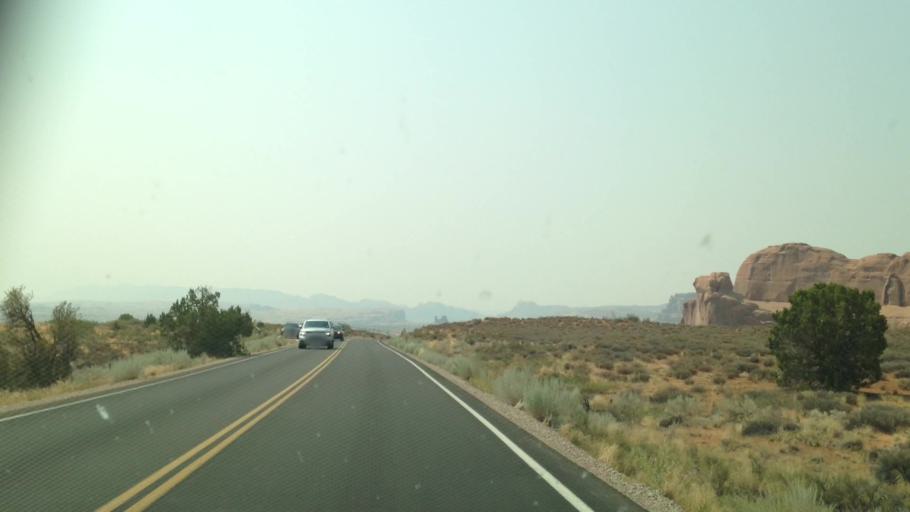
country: US
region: Utah
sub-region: Grand County
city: Moab
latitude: 38.6667
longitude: -109.5879
